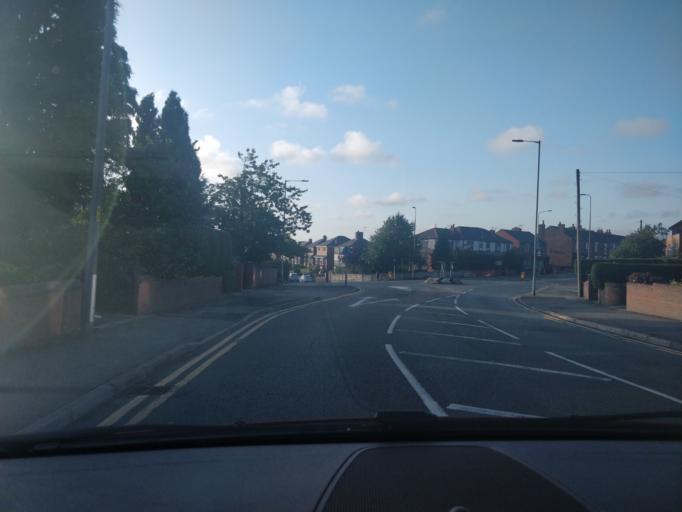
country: GB
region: England
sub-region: St. Helens
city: Billinge
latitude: 53.5255
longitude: -2.7161
